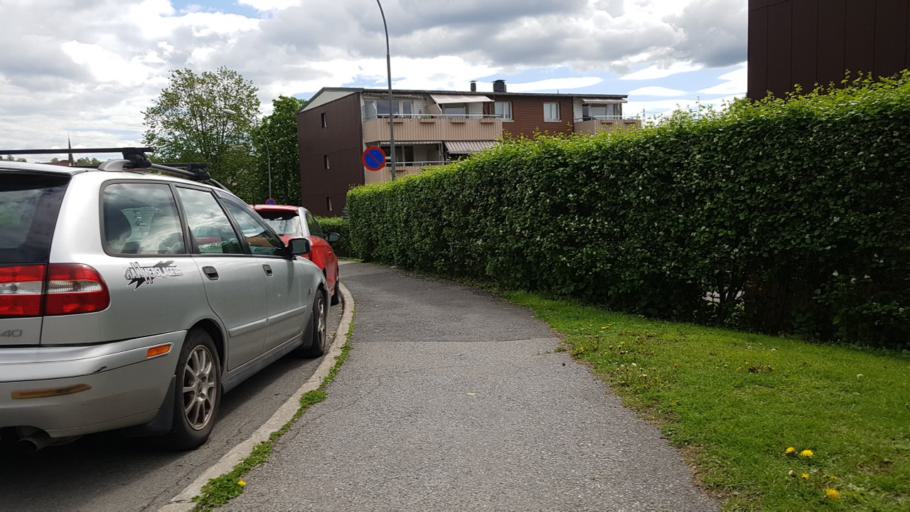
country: NO
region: Oslo
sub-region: Oslo
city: Oslo
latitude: 59.9415
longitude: 10.7930
